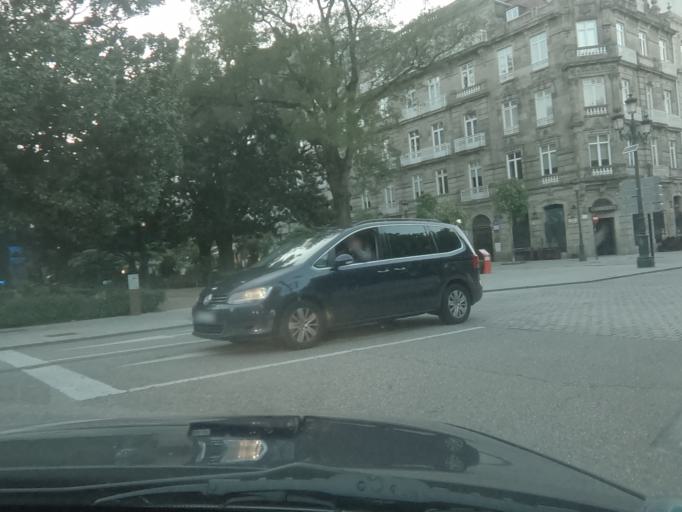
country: ES
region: Galicia
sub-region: Provincia de Pontevedra
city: Vigo
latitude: 42.2394
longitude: -8.7205
